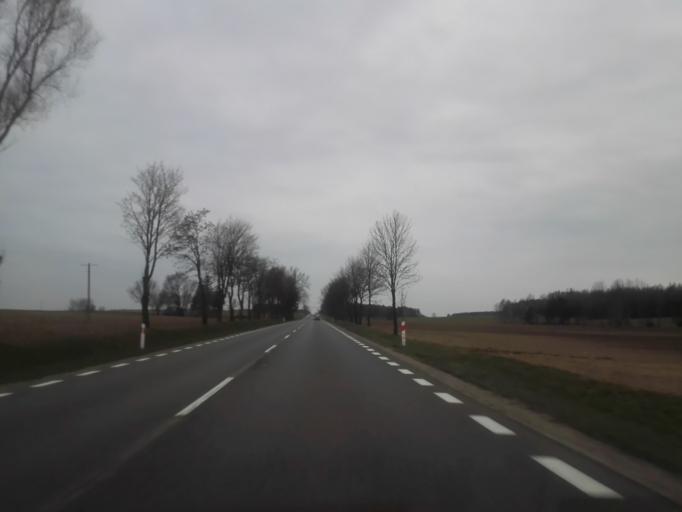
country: PL
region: Podlasie
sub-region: Powiat kolnenski
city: Stawiski
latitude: 53.4560
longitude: 22.1918
